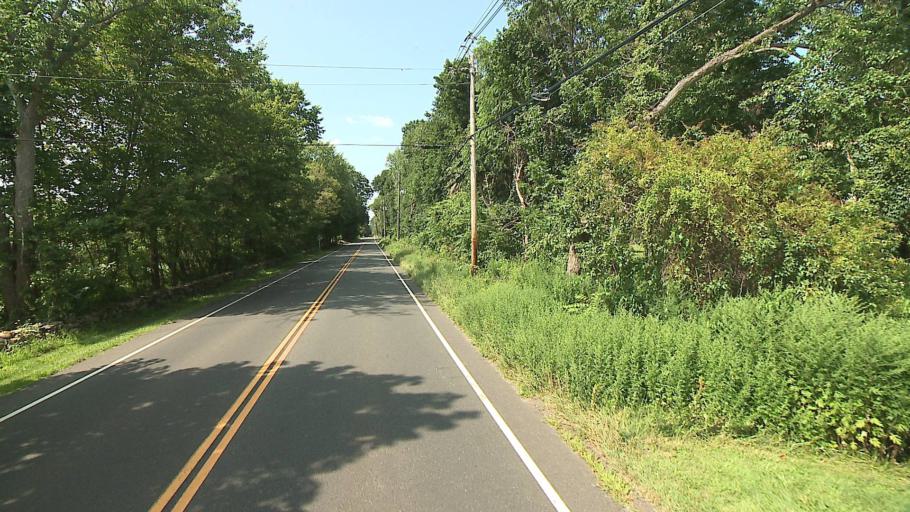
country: US
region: Connecticut
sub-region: Fairfield County
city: Newtown
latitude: 41.4495
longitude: -73.3770
